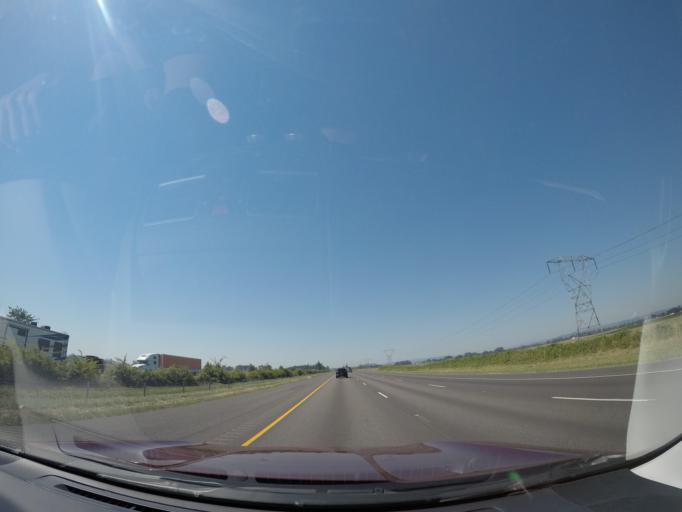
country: US
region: Oregon
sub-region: Marion County
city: Gervais
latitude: 45.0843
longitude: -122.9487
